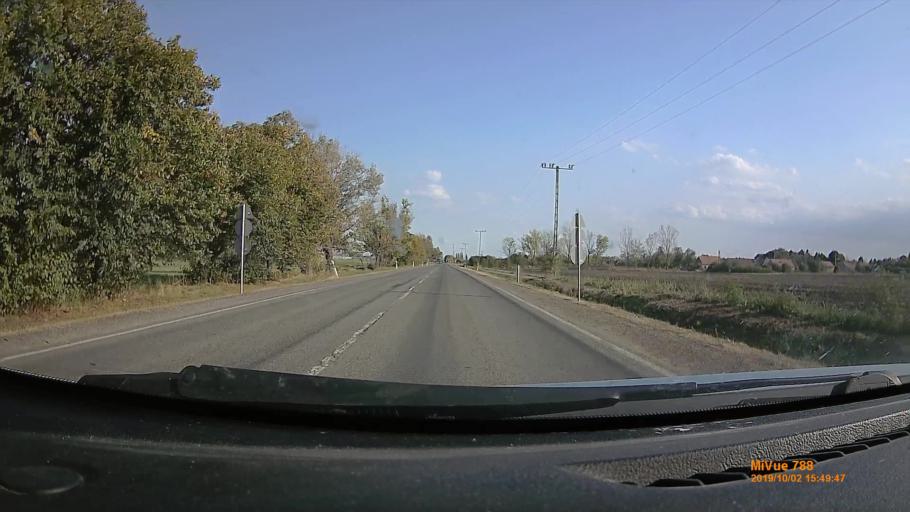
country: HU
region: Heves
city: Fuzesabony
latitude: 47.7711
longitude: 20.3809
